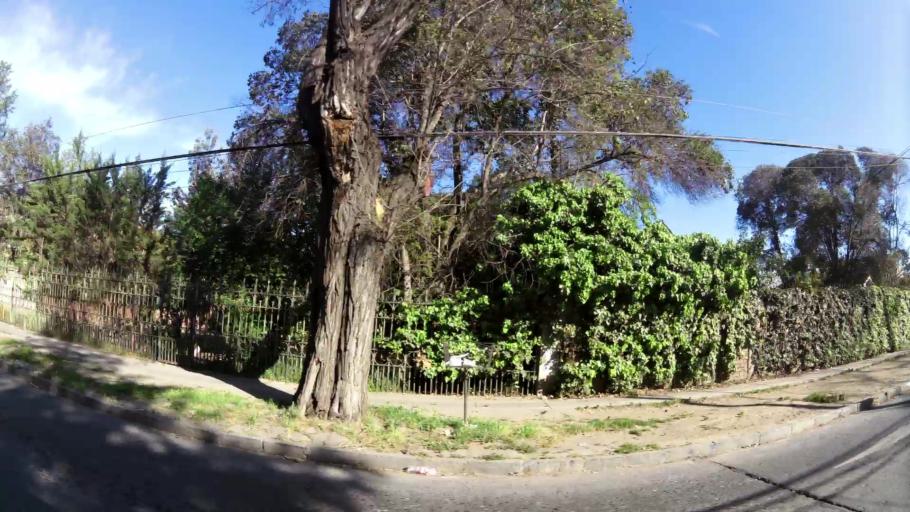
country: CL
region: Santiago Metropolitan
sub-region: Provincia de Santiago
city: Villa Presidente Frei, Nunoa, Santiago, Chile
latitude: -33.4384
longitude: -70.5517
